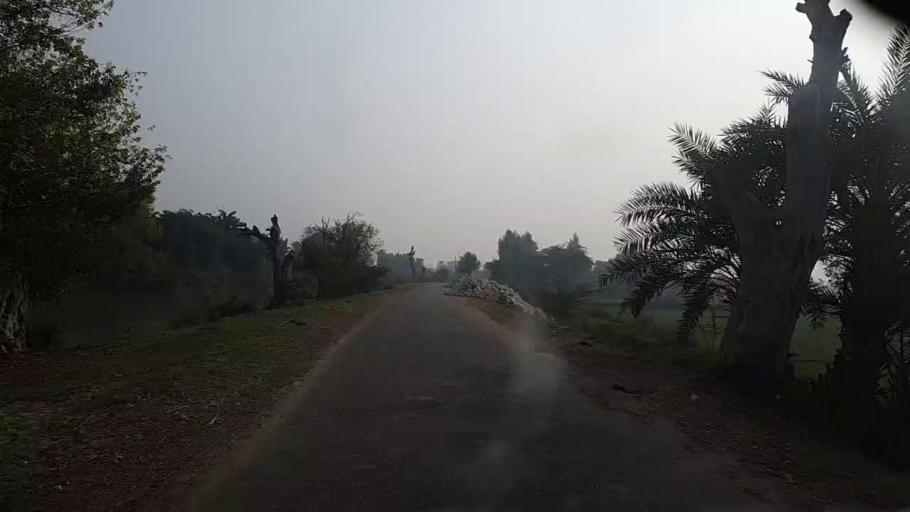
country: PK
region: Sindh
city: Bozdar
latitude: 27.1368
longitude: 68.6536
